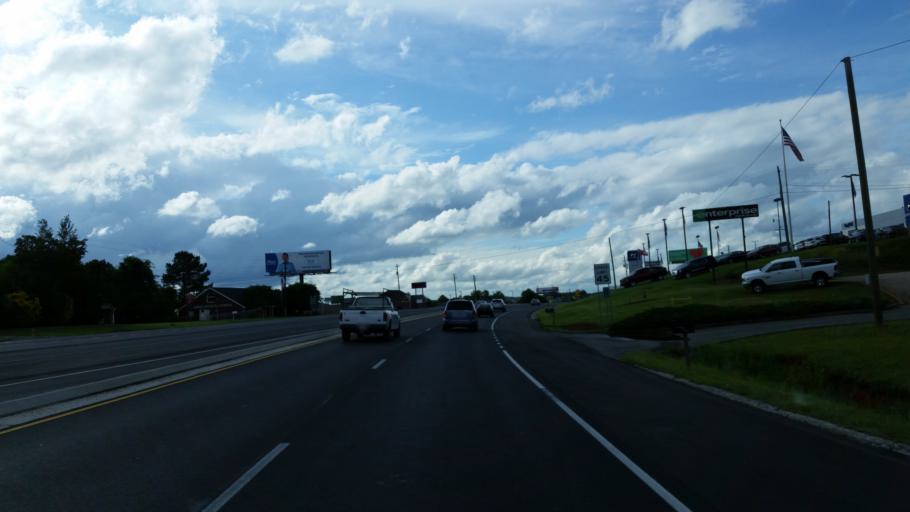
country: US
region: Georgia
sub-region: Bartow County
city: Cartersville
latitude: 34.1900
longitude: -84.7882
